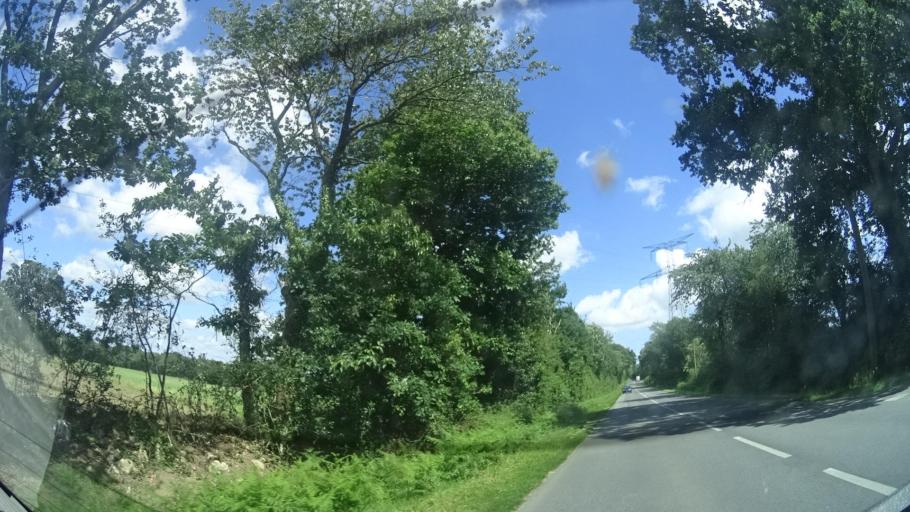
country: FR
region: Brittany
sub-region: Departement du Morbihan
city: Pluherlin
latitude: 47.6779
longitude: -2.3847
